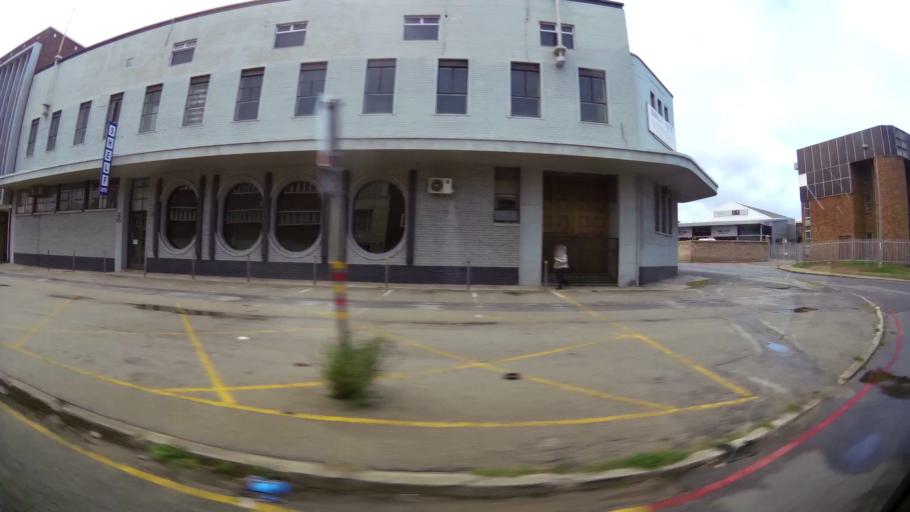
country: ZA
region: Eastern Cape
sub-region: Nelson Mandela Bay Metropolitan Municipality
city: Port Elizabeth
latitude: -33.9327
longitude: 25.6045
